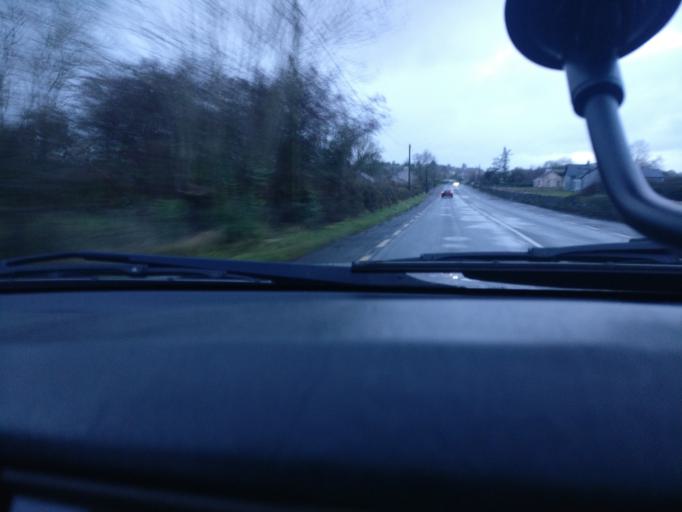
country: IE
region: Connaught
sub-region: County Galway
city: Ballinasloe
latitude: 53.3151
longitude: -8.2534
